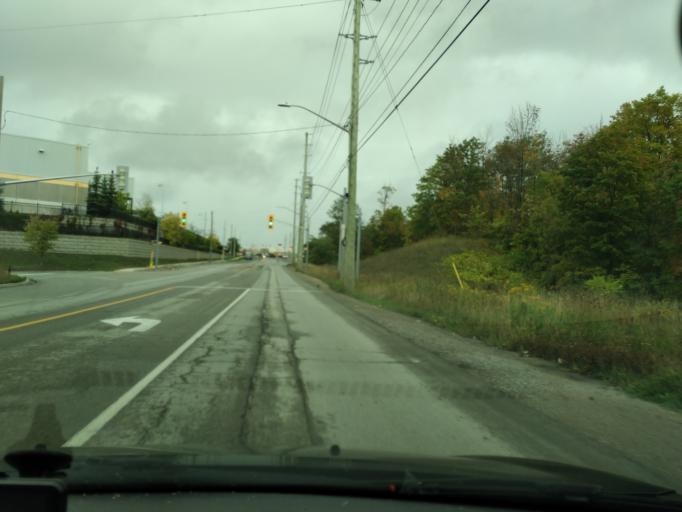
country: CA
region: Ontario
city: Innisfil
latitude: 44.3341
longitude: -79.6781
